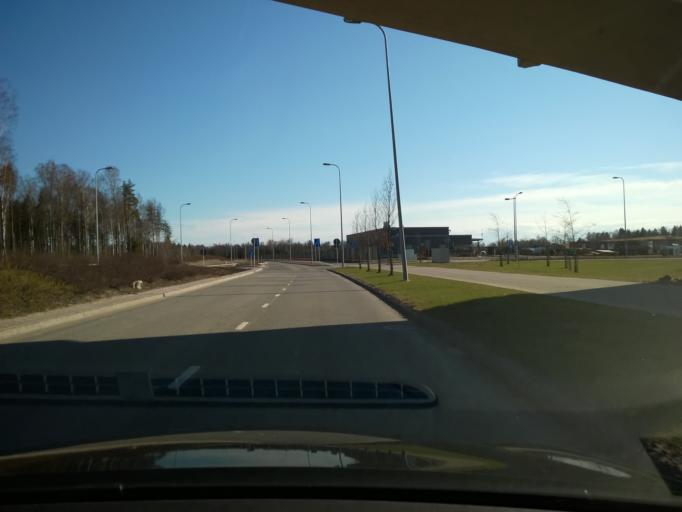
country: FI
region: Uusimaa
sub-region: Helsinki
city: Kilo
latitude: 60.1974
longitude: 24.7878
